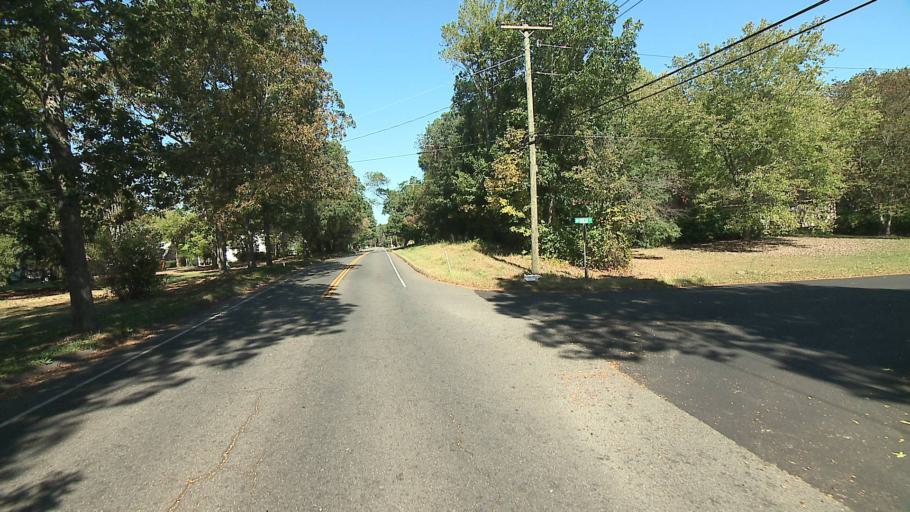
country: US
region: Connecticut
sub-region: New Haven County
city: Orange
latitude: 41.2605
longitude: -73.0515
